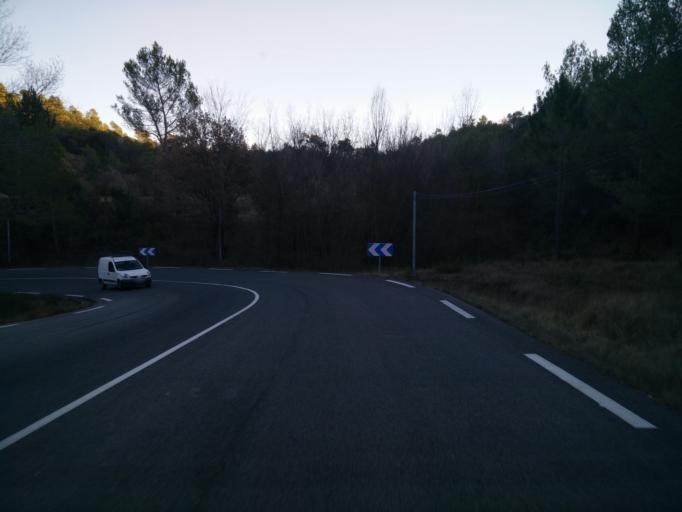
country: FR
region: Provence-Alpes-Cote d'Azur
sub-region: Departement du Var
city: Montferrat
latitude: 43.5911
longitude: 6.4702
